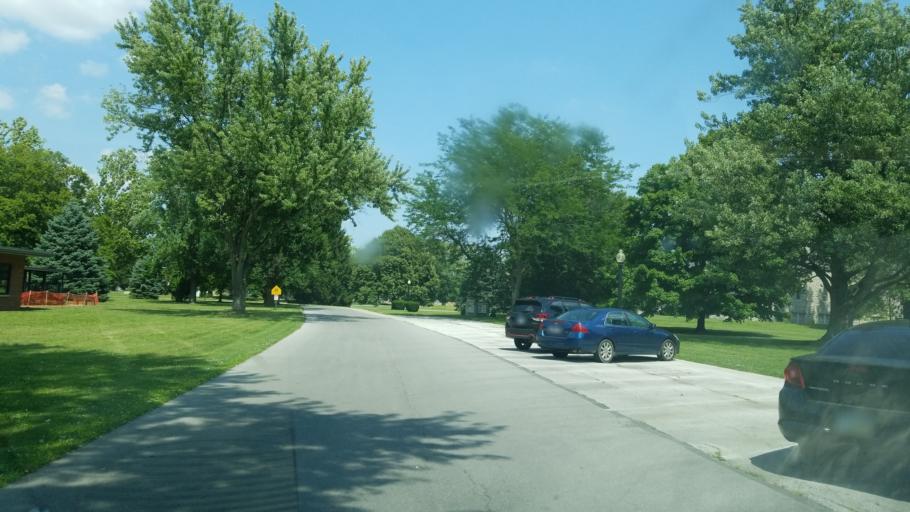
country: US
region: Ohio
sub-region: Seneca County
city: Tiffin
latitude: 41.1306
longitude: -83.1608
